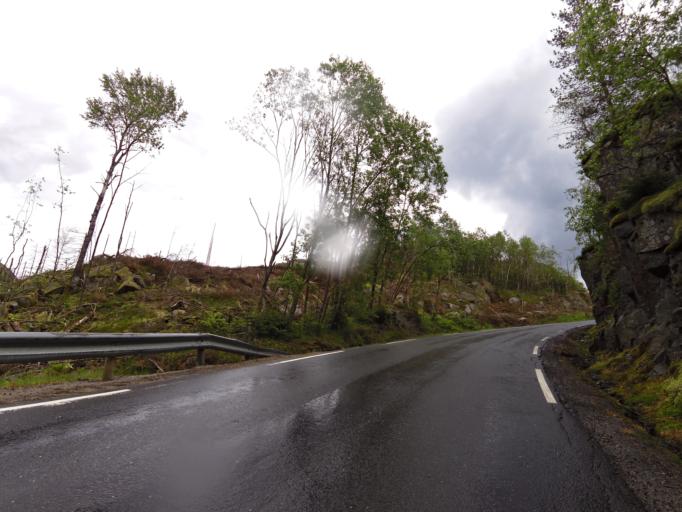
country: NO
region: Vest-Agder
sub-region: Lyngdal
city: Lyngdal
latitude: 58.1083
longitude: 7.0919
